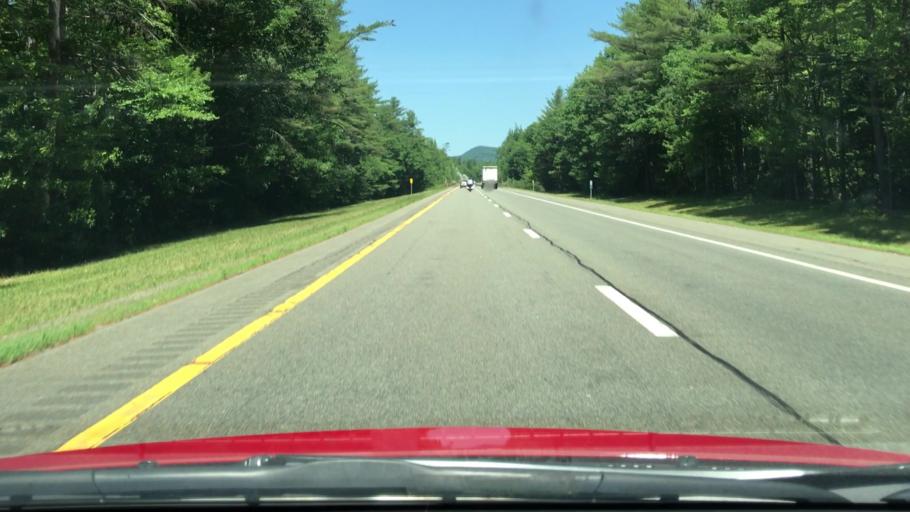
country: US
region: New York
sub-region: Essex County
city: Elizabethtown
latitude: 44.3296
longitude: -73.5310
